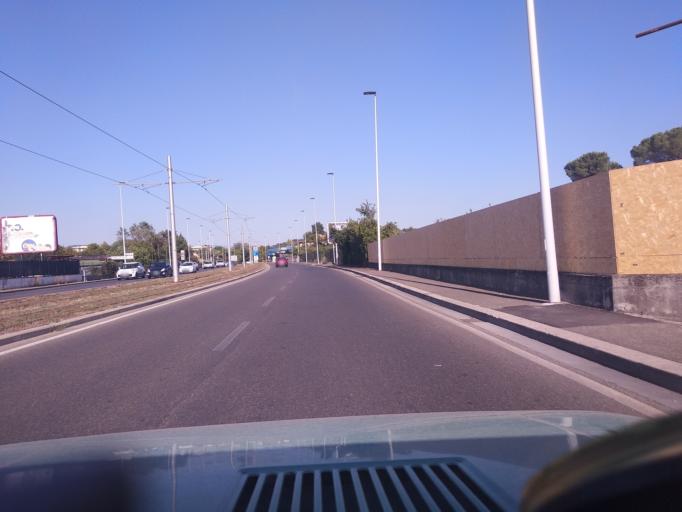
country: IT
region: Tuscany
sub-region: Province of Florence
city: Scandicci
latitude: 43.7647
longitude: 11.2033
